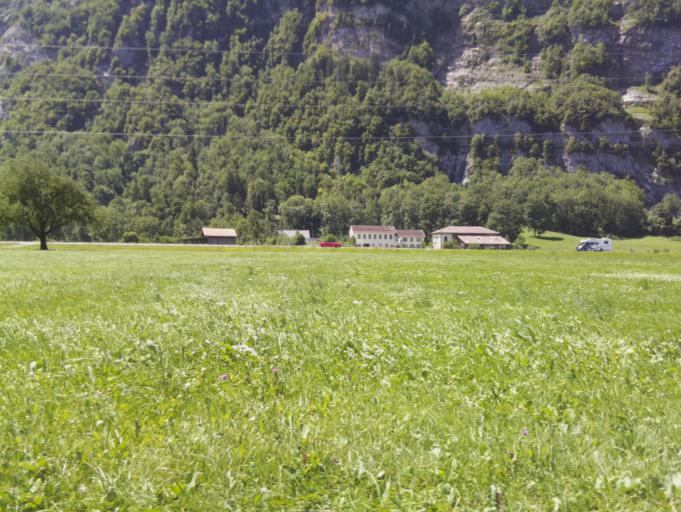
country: CH
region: Glarus
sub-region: Glarus
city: Netstal
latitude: 47.0787
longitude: 9.0569
